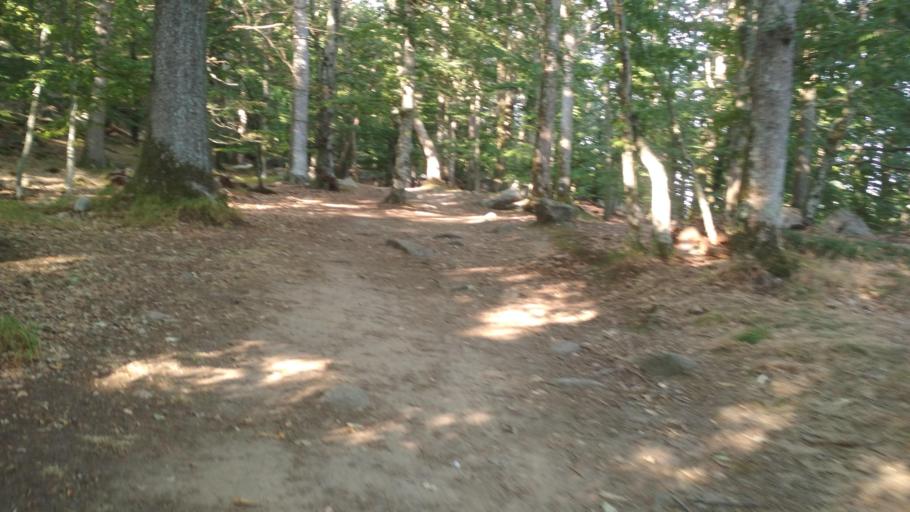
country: DK
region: Capital Region
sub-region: Bornholm Kommune
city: Akirkeby
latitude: 55.1079
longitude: 14.8976
